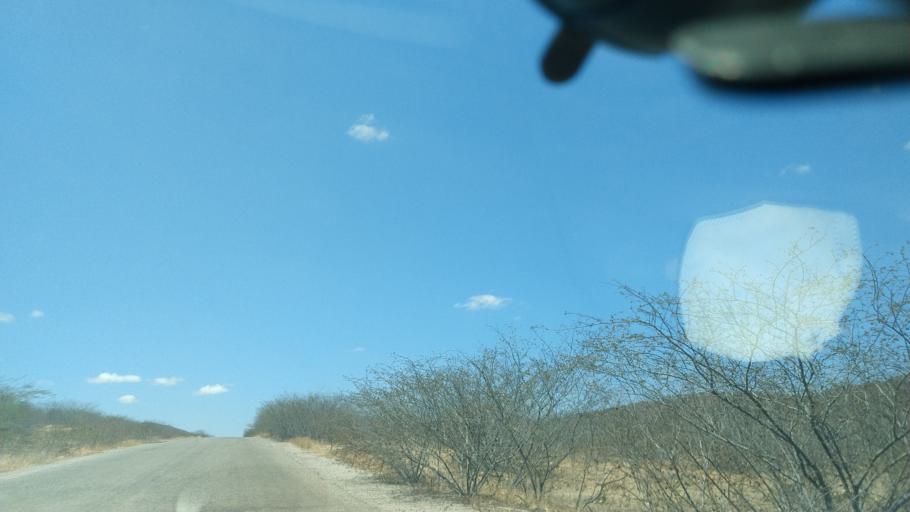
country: BR
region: Rio Grande do Norte
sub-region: Sao Tome
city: Sao Tome
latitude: -5.9707
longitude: -36.1334
